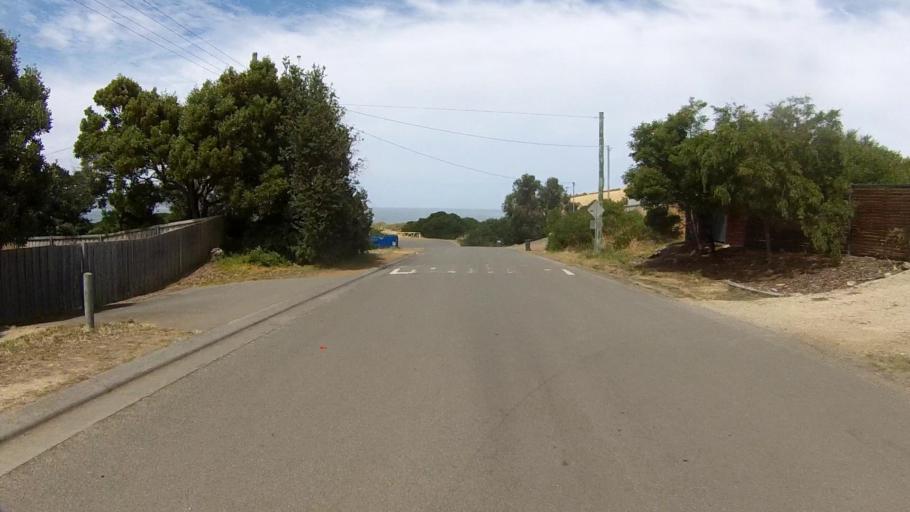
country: AU
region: Tasmania
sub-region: Clarence
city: Sandford
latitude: -42.9913
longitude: 147.5233
